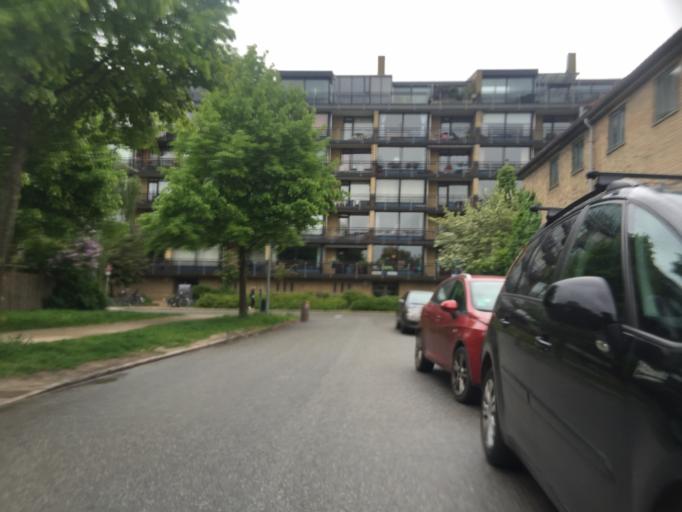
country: DK
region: Capital Region
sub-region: Frederiksberg Kommune
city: Frederiksberg
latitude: 55.6898
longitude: 12.5270
